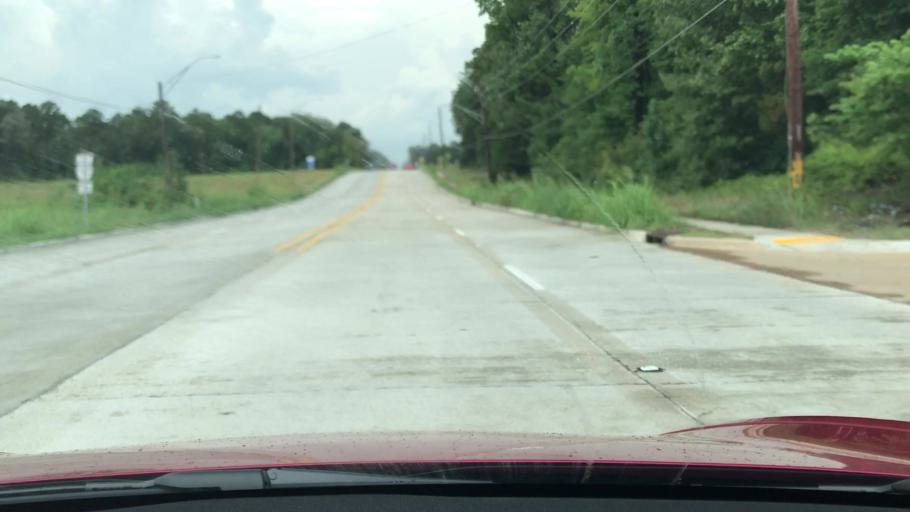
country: US
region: Louisiana
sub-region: Bossier Parish
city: Bossier City
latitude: 32.4000
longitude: -93.7633
